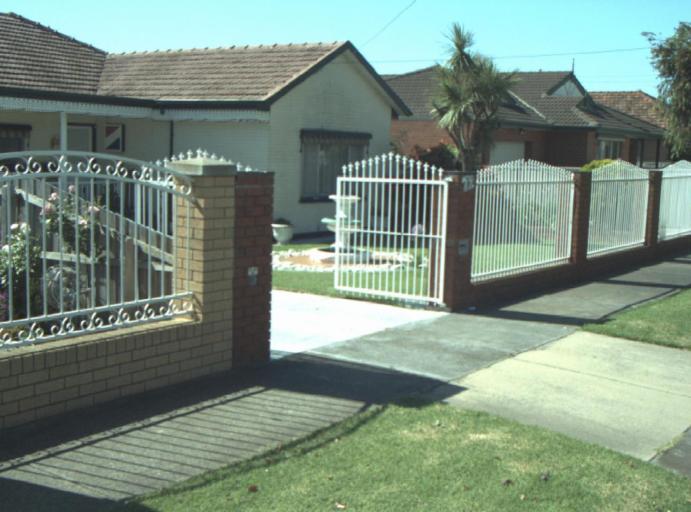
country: AU
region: Victoria
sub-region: Greater Geelong
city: Bell Park
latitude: -38.1111
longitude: 144.3374
